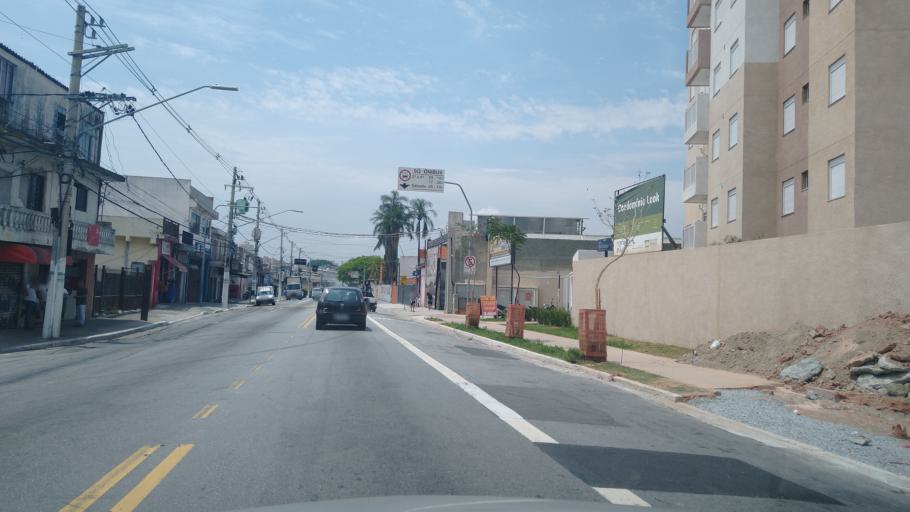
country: BR
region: Sao Paulo
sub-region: Sao Paulo
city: Sao Paulo
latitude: -23.4719
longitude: -46.6741
